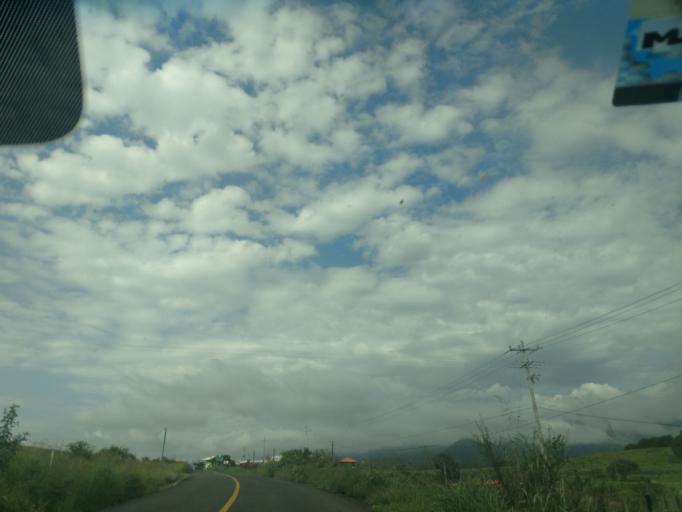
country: MX
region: Jalisco
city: El Salto
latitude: 20.4283
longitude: -104.4950
